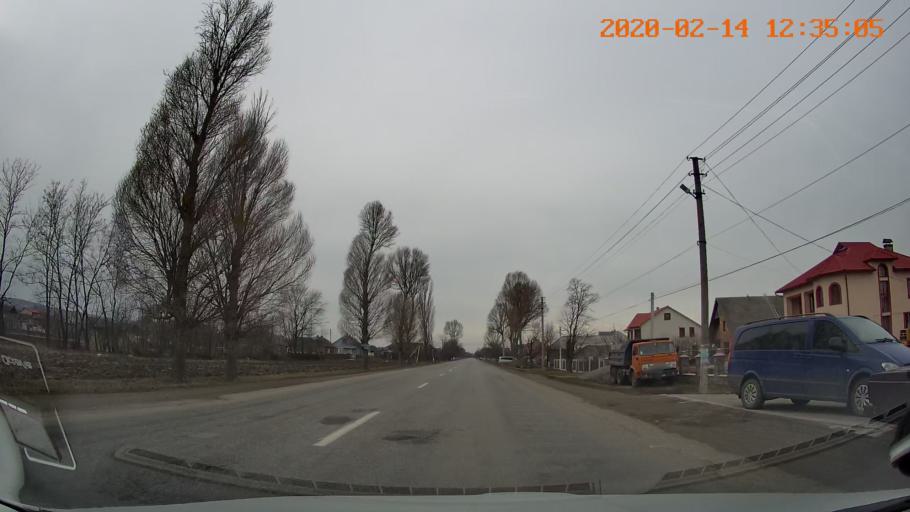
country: RO
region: Botosani
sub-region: Comuna Darabani
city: Bajura
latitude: 48.2271
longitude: 26.5204
